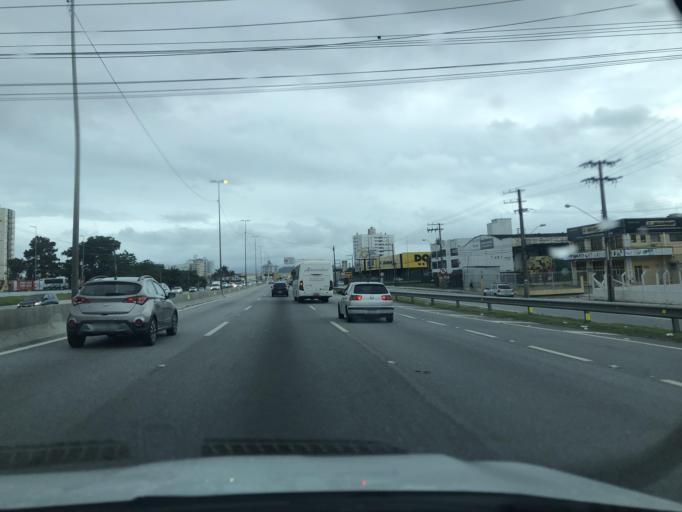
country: BR
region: Santa Catarina
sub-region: Sao Jose
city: Campinas
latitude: -27.5903
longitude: -48.6177
